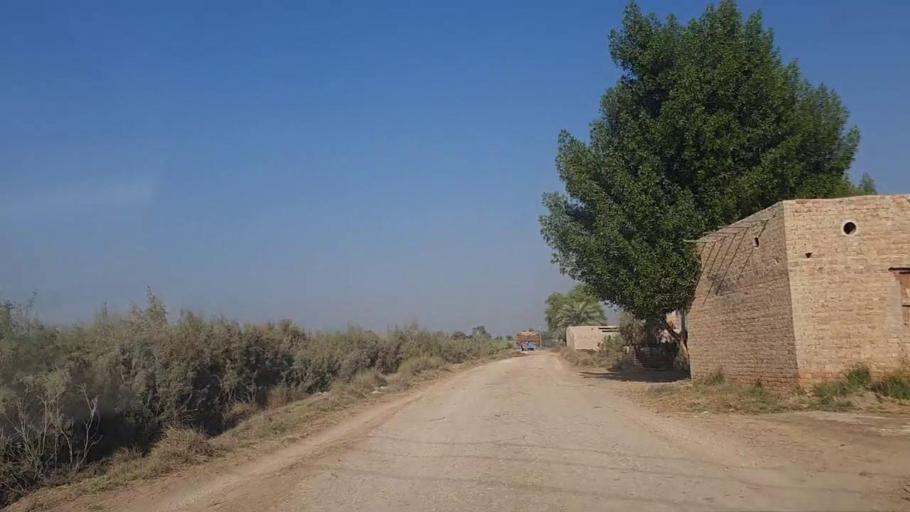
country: PK
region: Sindh
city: Gambat
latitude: 27.3614
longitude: 68.4742
